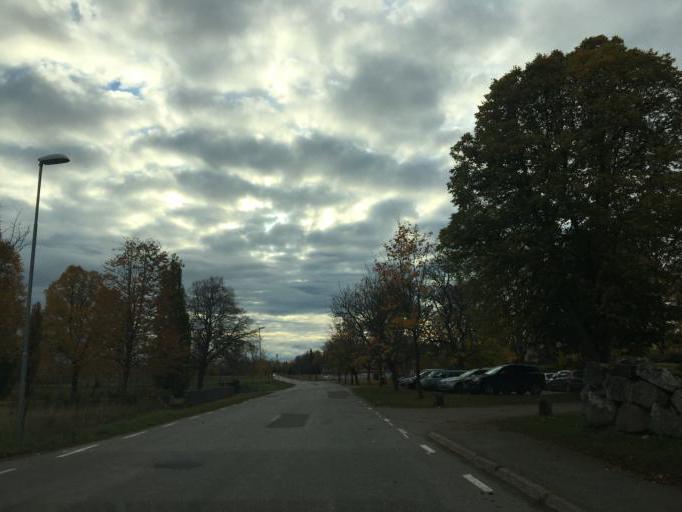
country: SE
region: Soedermanland
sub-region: Eskilstuna Kommun
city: Kvicksund
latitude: 59.5694
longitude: 16.4029
